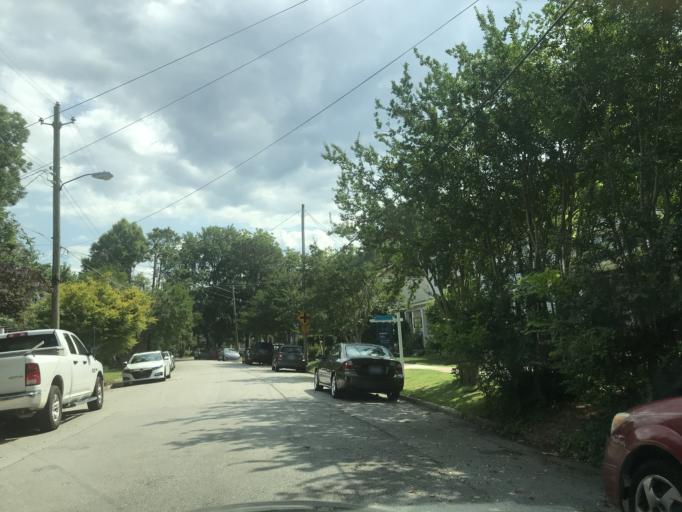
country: US
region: North Carolina
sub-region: Wake County
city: Raleigh
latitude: 35.7767
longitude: -78.6519
